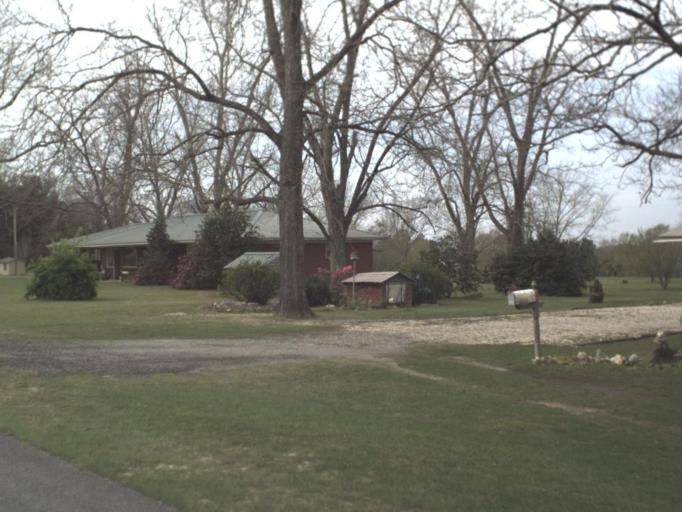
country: US
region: Florida
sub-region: Holmes County
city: Bonifay
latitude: 30.9100
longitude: -85.6504
